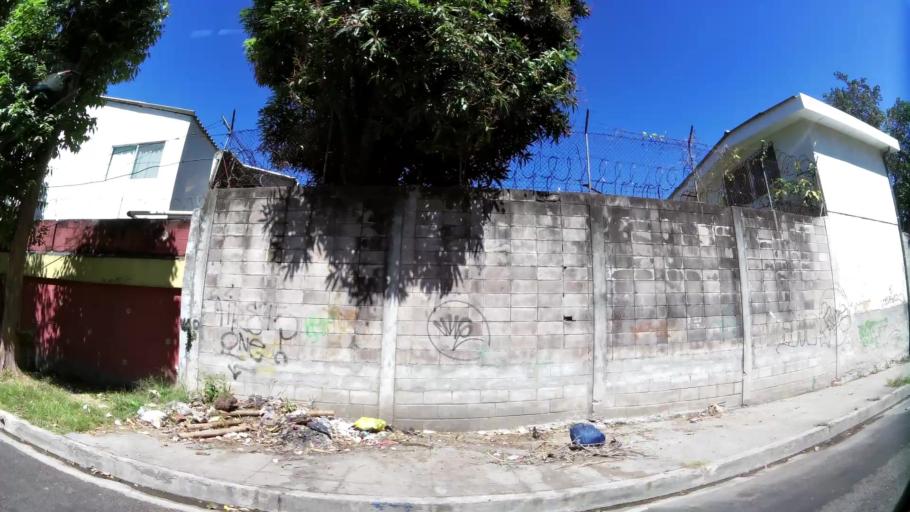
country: SV
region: La Libertad
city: Santa Tecla
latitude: 13.6707
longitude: -89.2806
